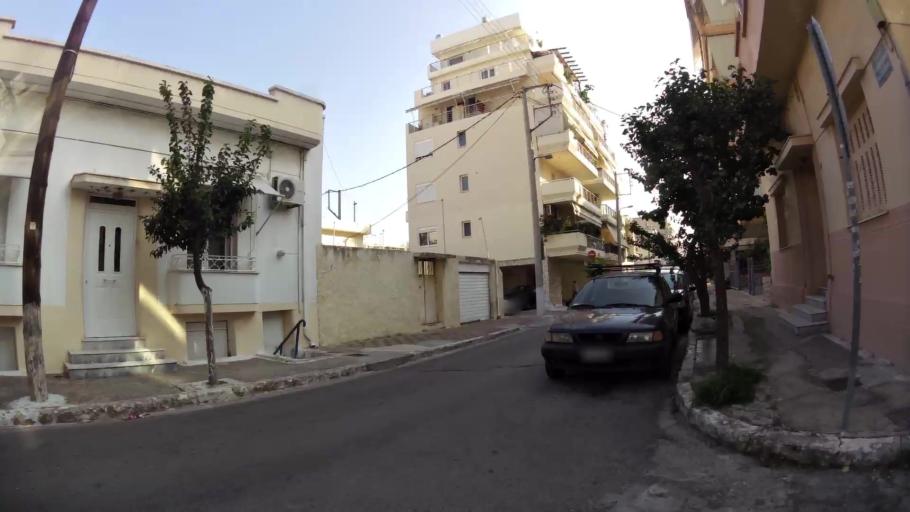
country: GR
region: Attica
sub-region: Nomos Piraios
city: Drapetsona
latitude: 37.9450
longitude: 23.6222
